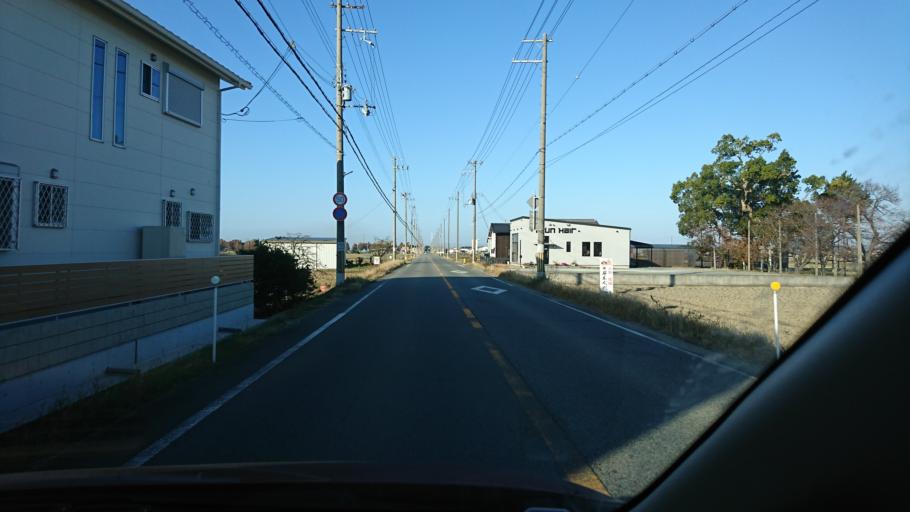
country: JP
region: Hyogo
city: Miki
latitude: 34.7339
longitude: 134.9182
